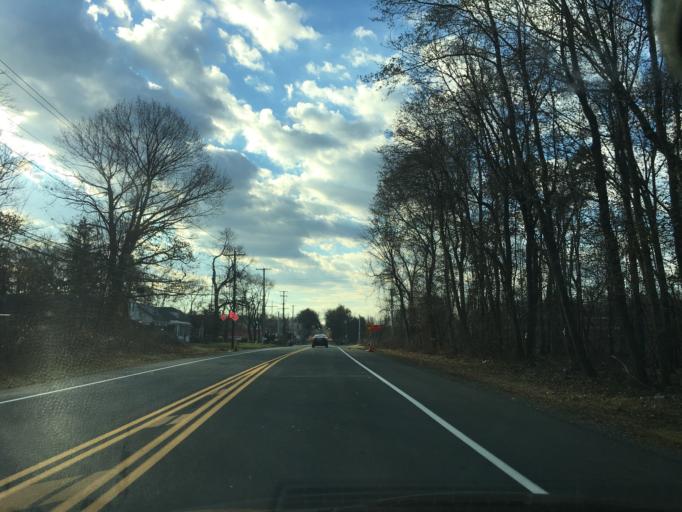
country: US
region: New York
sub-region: Albany County
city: Menands
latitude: 42.6746
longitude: -73.6912
